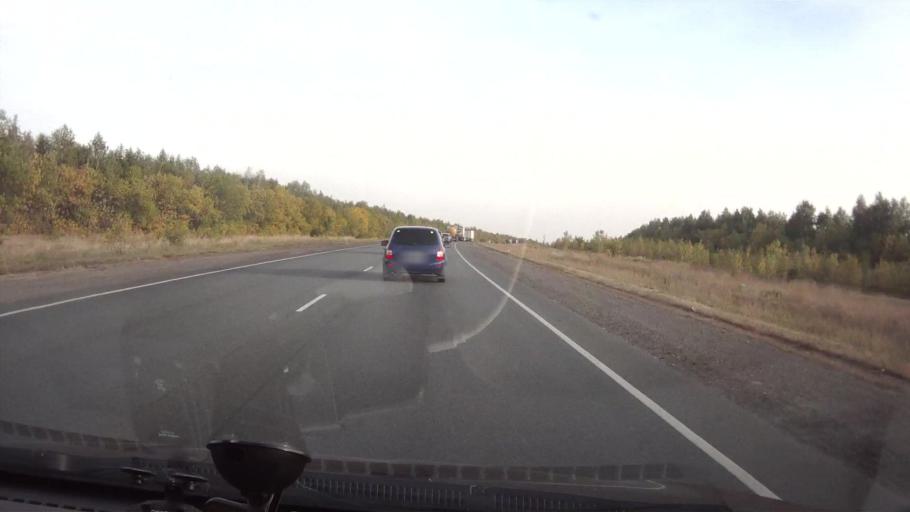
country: RU
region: Saratov
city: Sokolovyy
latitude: 51.5312
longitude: 45.8039
